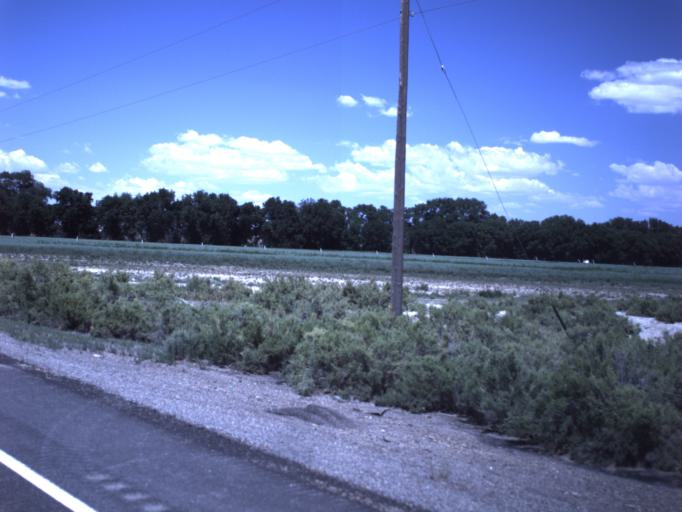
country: US
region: Utah
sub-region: Emery County
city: Huntington
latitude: 39.3021
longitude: -110.9642
